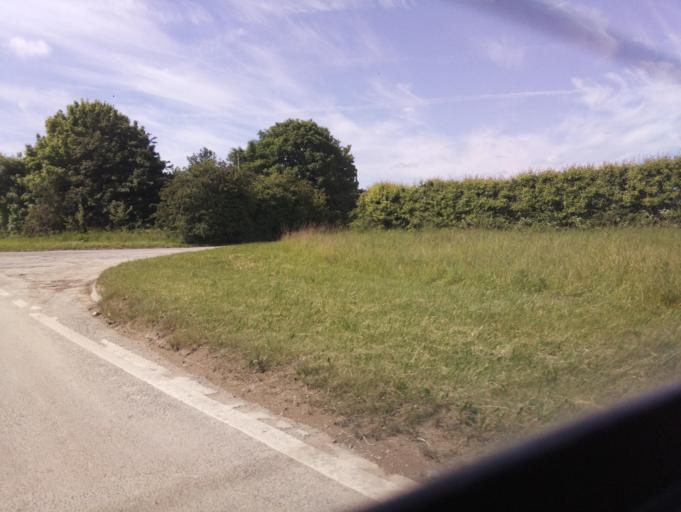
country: GB
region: England
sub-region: North Lincolnshire
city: Manton
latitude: 53.5132
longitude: -0.5802
